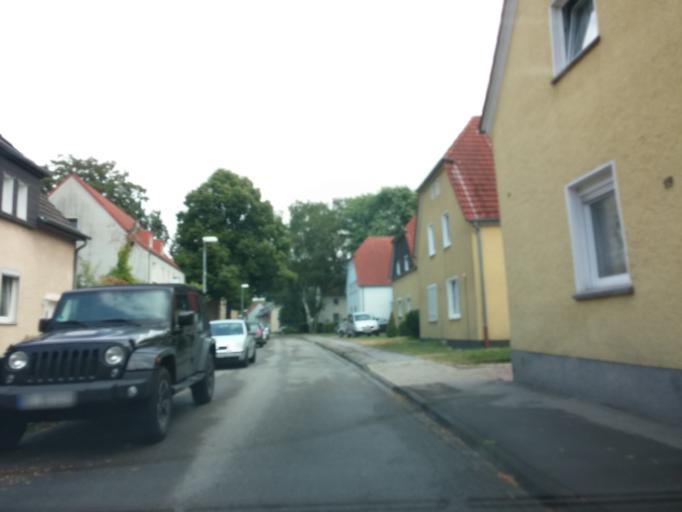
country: DE
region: North Rhine-Westphalia
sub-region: Regierungsbezirk Munster
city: Gladbeck
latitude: 51.5923
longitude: 7.0152
